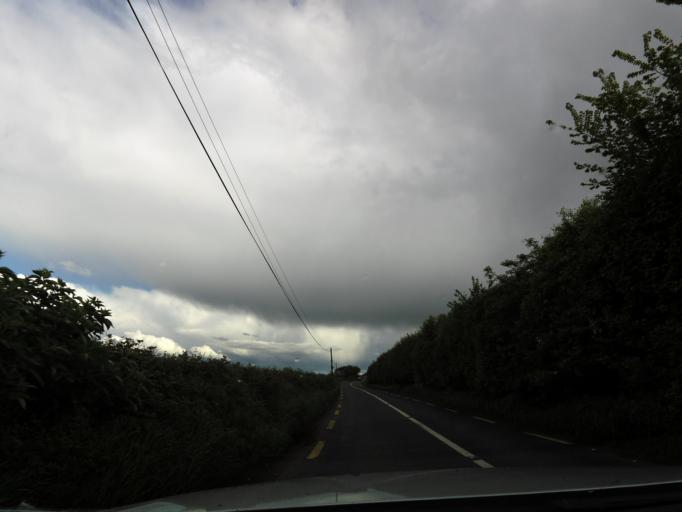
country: IE
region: Munster
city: Thurles
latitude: 52.7232
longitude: -7.8338
